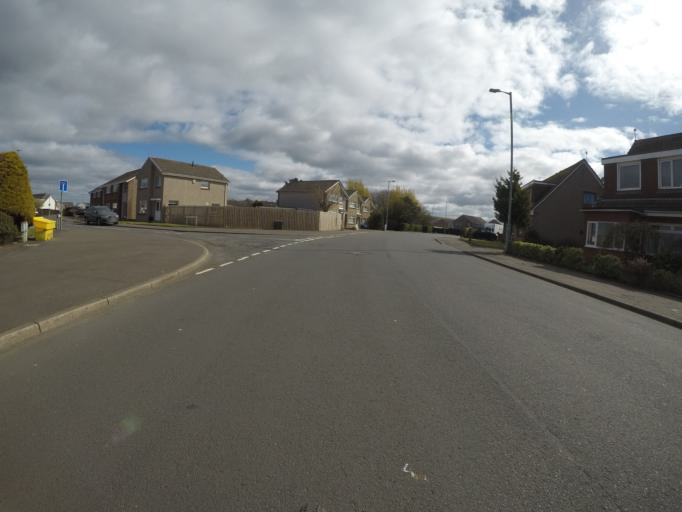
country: GB
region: Scotland
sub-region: South Ayrshire
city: Troon
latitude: 55.5648
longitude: -4.6441
